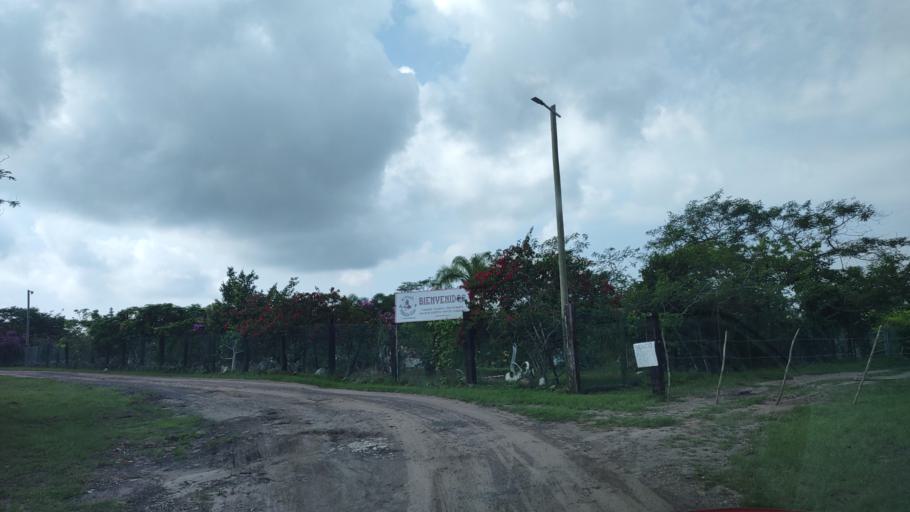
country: MX
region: Veracruz
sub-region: Emiliano Zapata
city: Dos Rios
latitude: 19.4515
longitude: -96.8111
